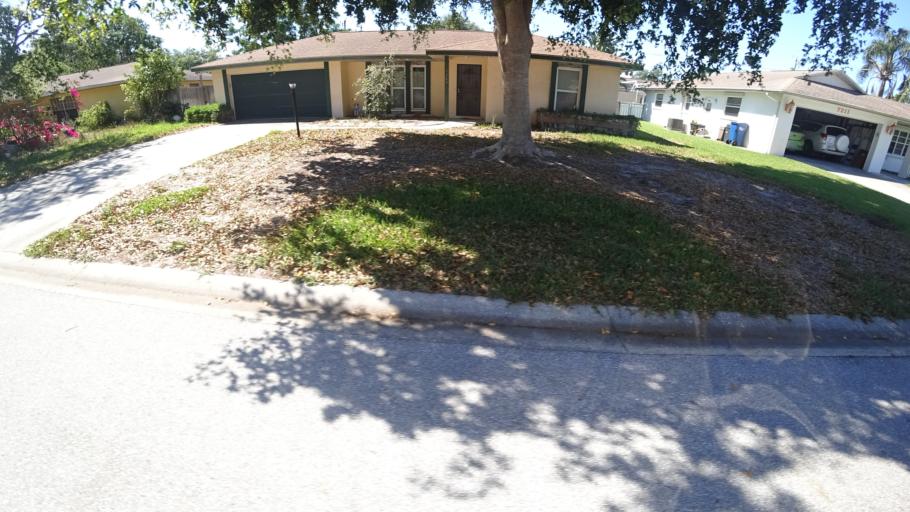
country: US
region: Florida
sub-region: Manatee County
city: West Bradenton
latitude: 27.4790
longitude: -82.6341
